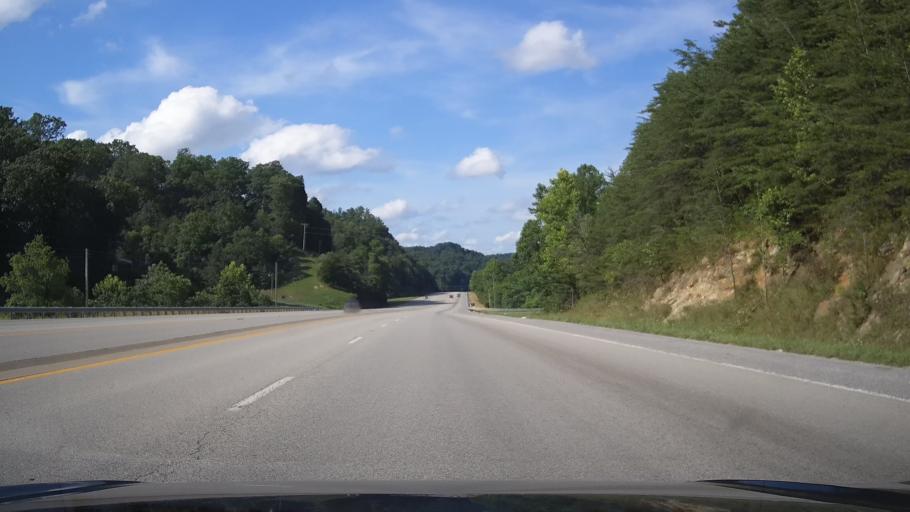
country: US
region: Kentucky
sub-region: Lawrence County
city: Louisa
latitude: 38.0393
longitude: -82.6492
